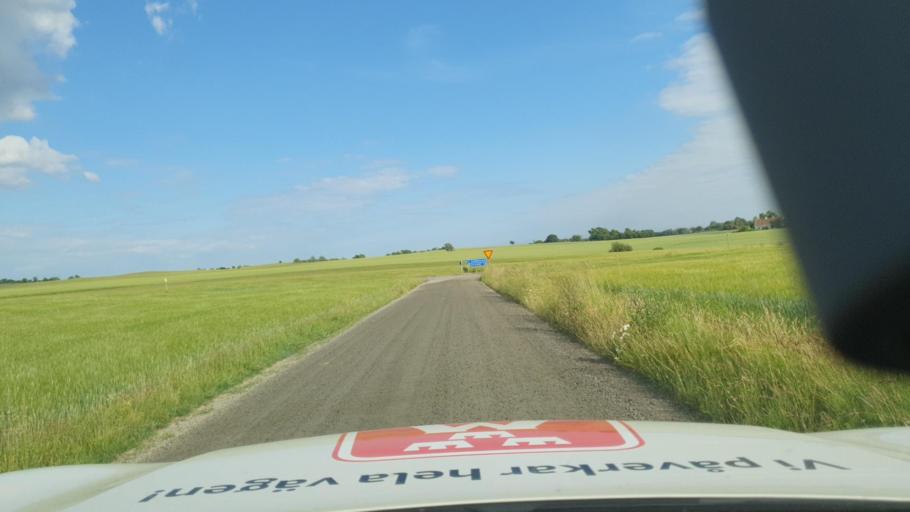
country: SE
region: Skane
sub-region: Skurups Kommun
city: Skivarp
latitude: 55.4325
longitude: 13.5970
